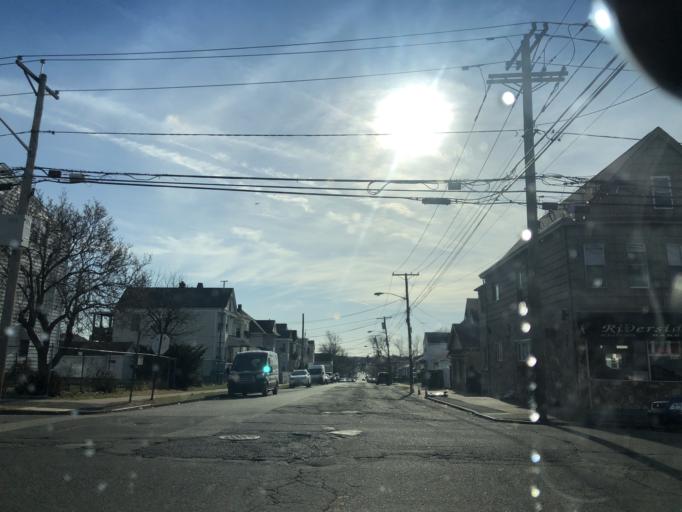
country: US
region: New Jersey
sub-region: Bergen County
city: Fair Lawn
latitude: 40.9319
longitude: -74.1476
